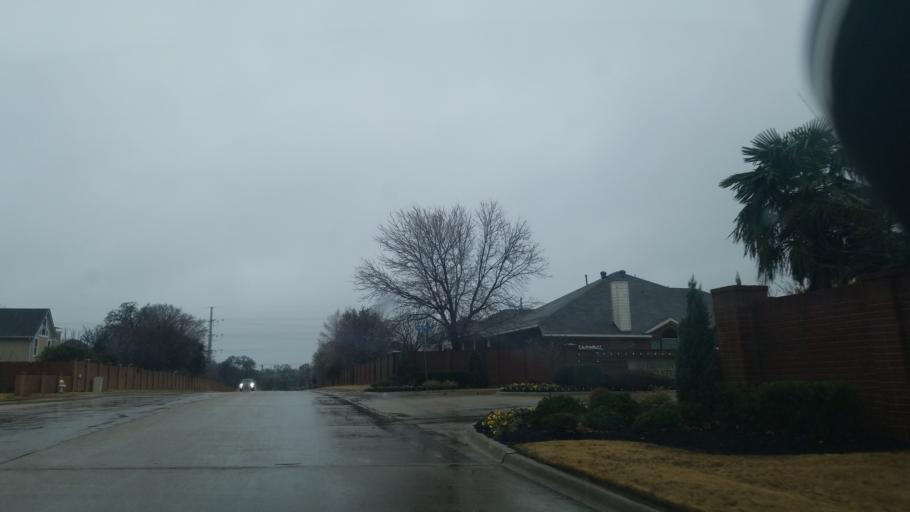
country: US
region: Texas
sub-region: Denton County
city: Corinth
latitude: 33.1614
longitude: -97.0885
